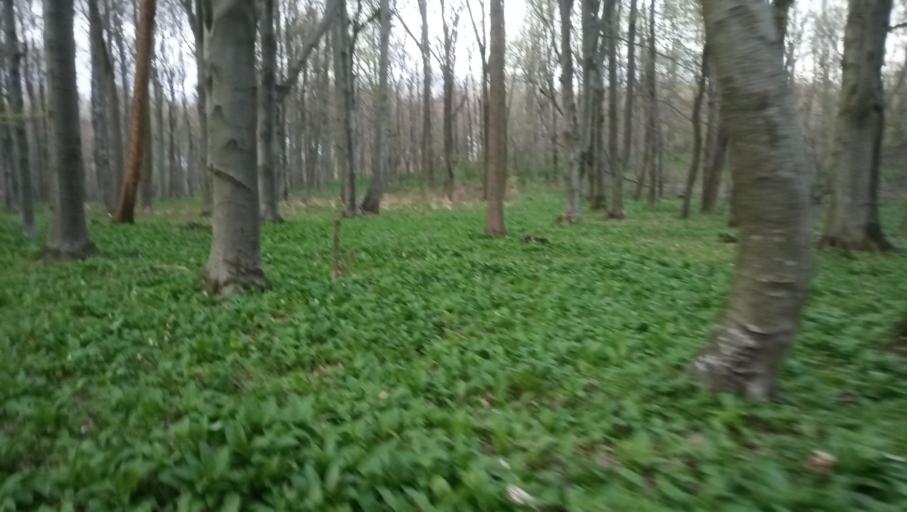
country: HU
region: Veszprem
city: Herend
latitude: 47.1882
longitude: 17.7464
